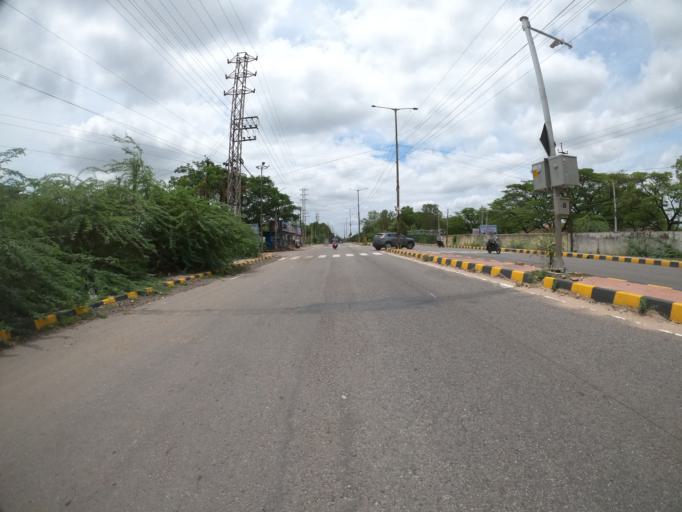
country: IN
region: Telangana
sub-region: Hyderabad
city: Hyderabad
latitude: 17.3768
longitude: 78.3830
